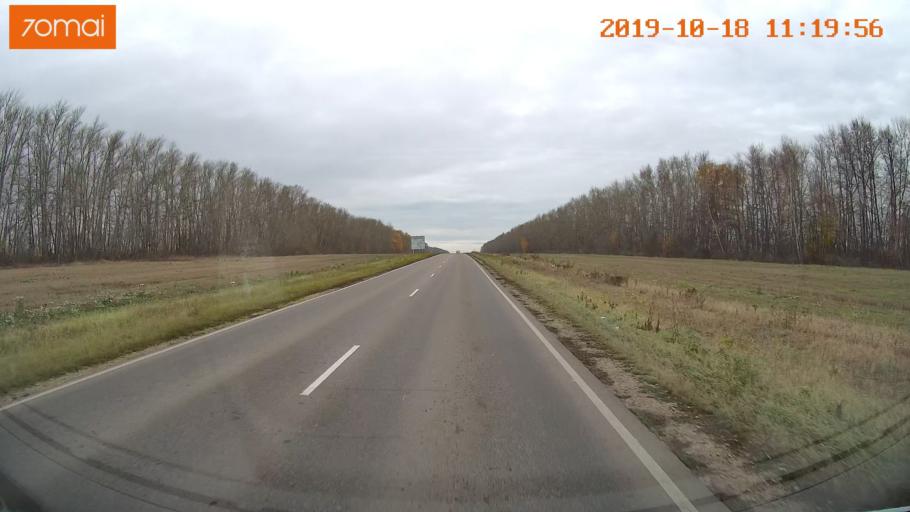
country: RU
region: Tula
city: Kimovsk
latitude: 54.0527
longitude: 38.5562
